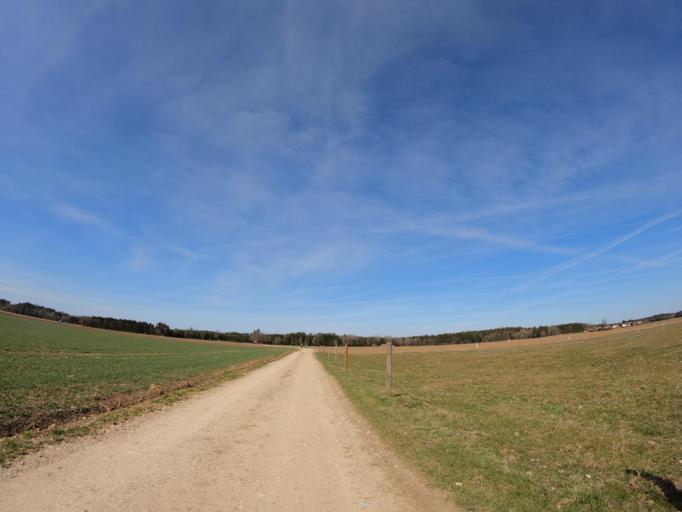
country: DE
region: Bavaria
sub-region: Upper Bavaria
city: Brunnthal
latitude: 47.9889
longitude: 11.7018
